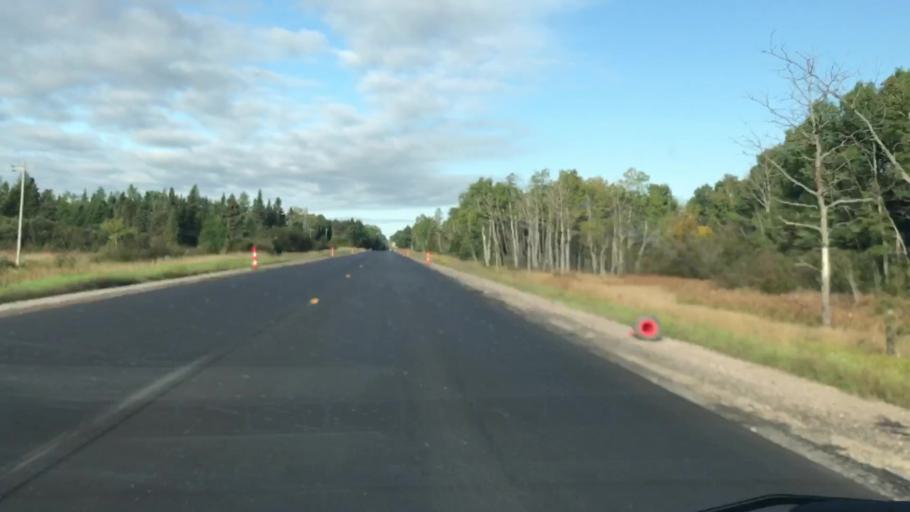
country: US
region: Michigan
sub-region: Mackinac County
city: Saint Ignace
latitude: 46.3460
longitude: -84.9484
